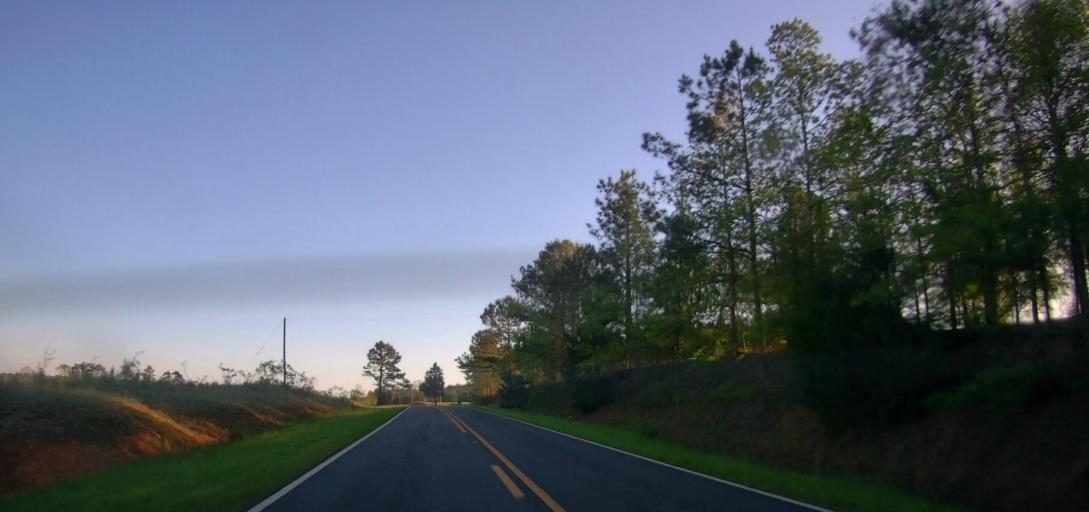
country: US
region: Georgia
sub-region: Marion County
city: Buena Vista
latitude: 32.4427
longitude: -84.4269
